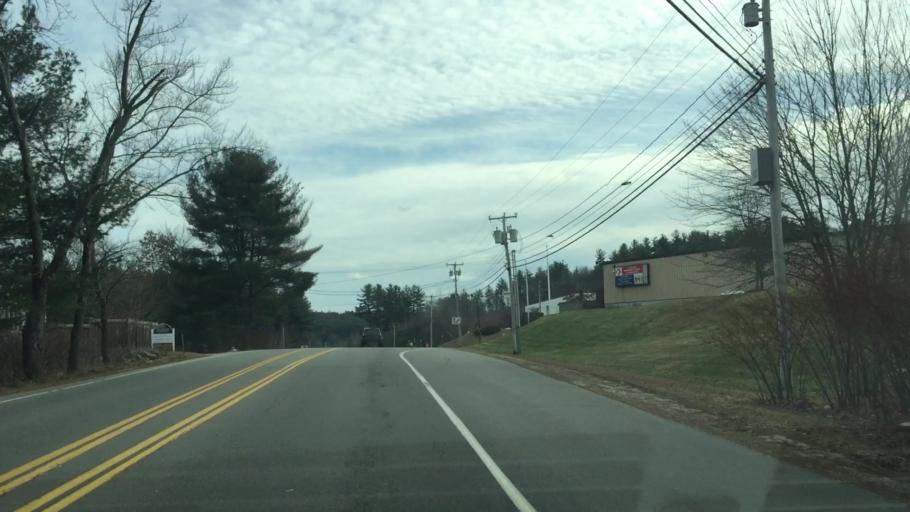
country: US
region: New Hampshire
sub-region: Hillsborough County
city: Manchester
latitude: 42.9380
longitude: -71.4192
